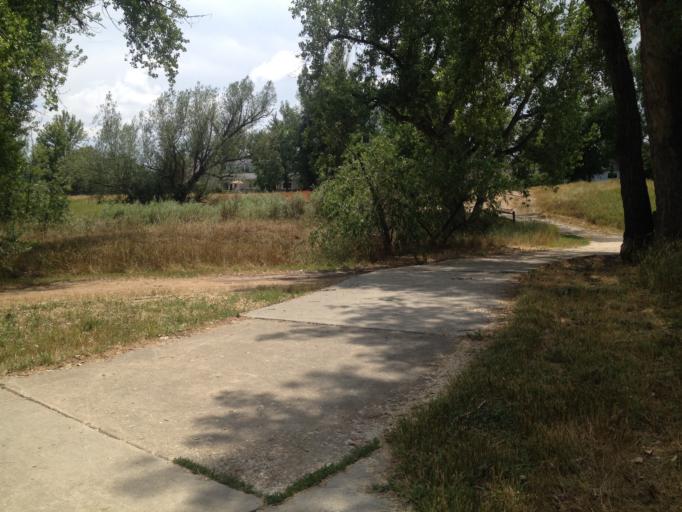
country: US
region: Colorado
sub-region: Boulder County
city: Louisville
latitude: 39.9725
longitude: -105.1488
